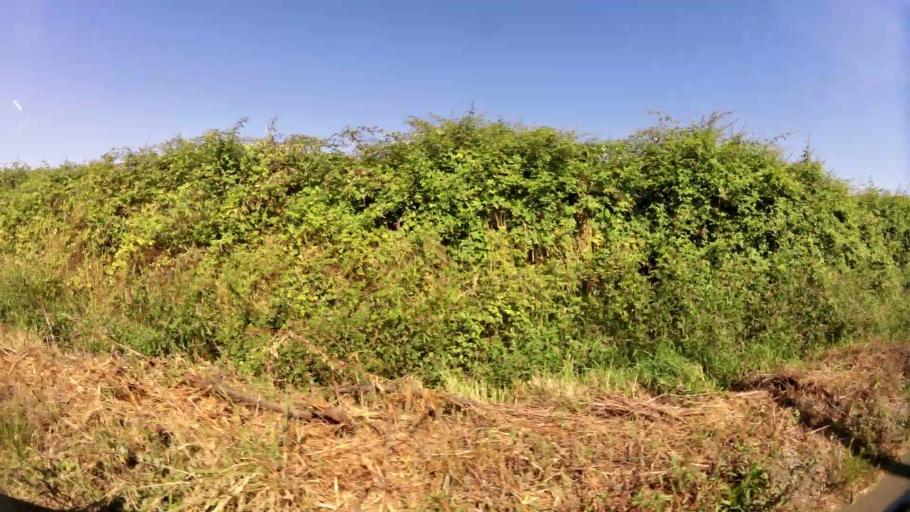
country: CL
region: Maule
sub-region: Provincia de Talca
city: Talca
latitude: -35.4122
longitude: -71.5929
